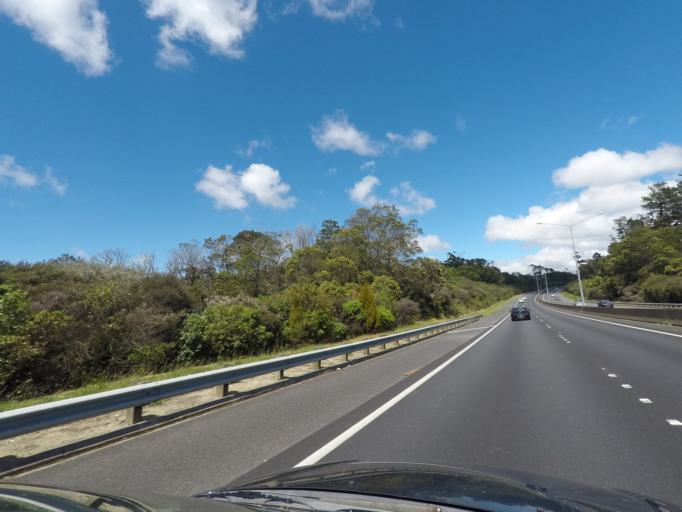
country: NZ
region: Auckland
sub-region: Auckland
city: North Shore
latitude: -36.7723
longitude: 174.6856
